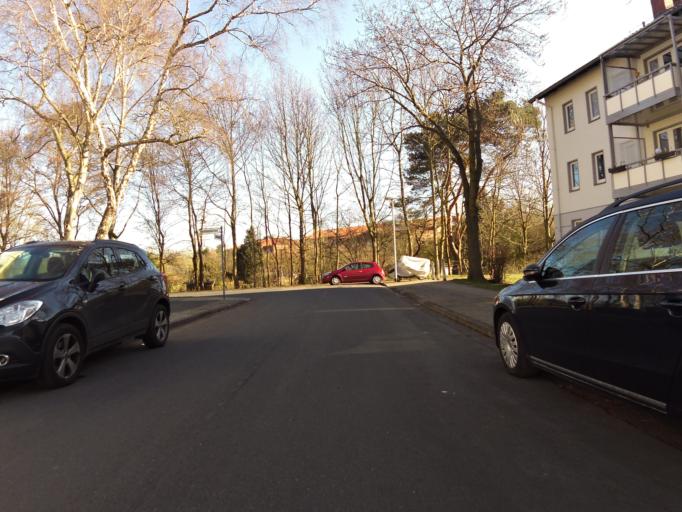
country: DE
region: Lower Saxony
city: Hannover
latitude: 52.3780
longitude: 9.7938
